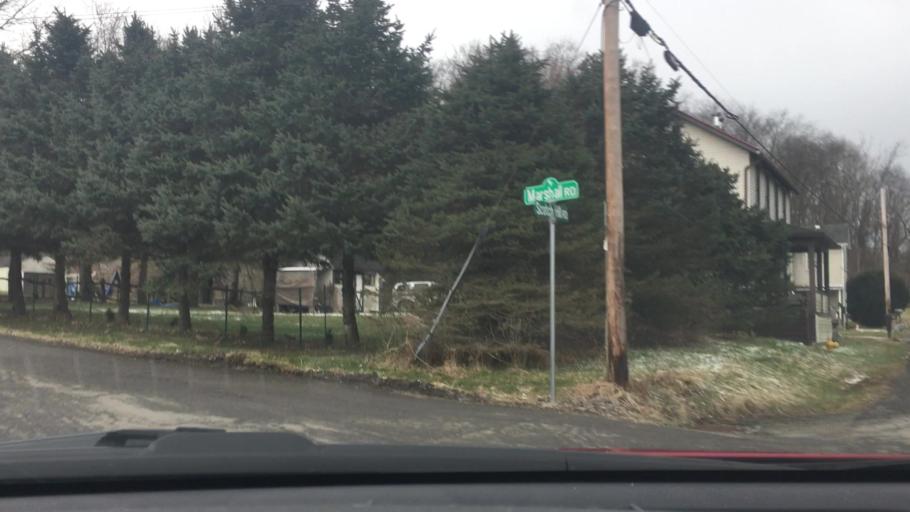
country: US
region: Pennsylvania
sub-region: Allegheny County
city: Sturgeon
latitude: 40.3890
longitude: -80.1989
